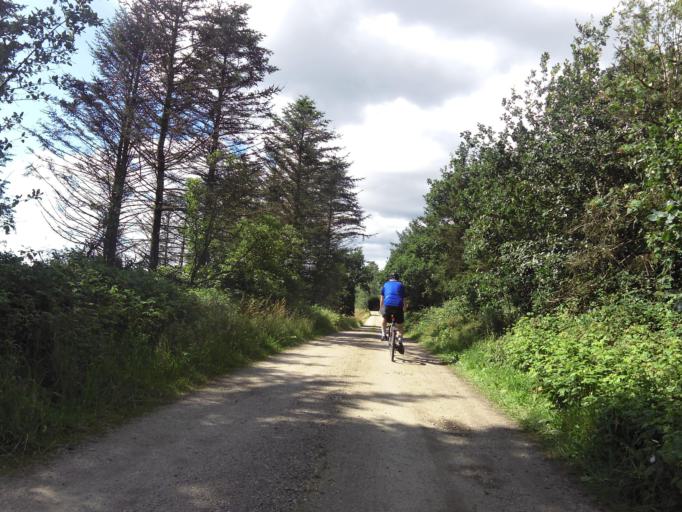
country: DK
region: South Denmark
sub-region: Haderslev Kommune
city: Vojens
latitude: 55.3179
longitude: 9.2003
